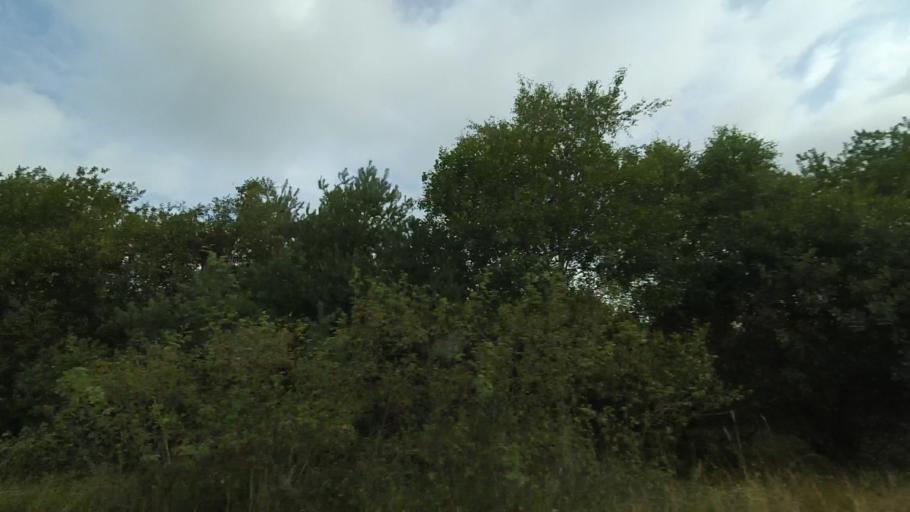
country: DK
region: Central Jutland
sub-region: Syddjurs Kommune
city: Ryomgard
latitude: 56.3994
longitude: 10.4932
